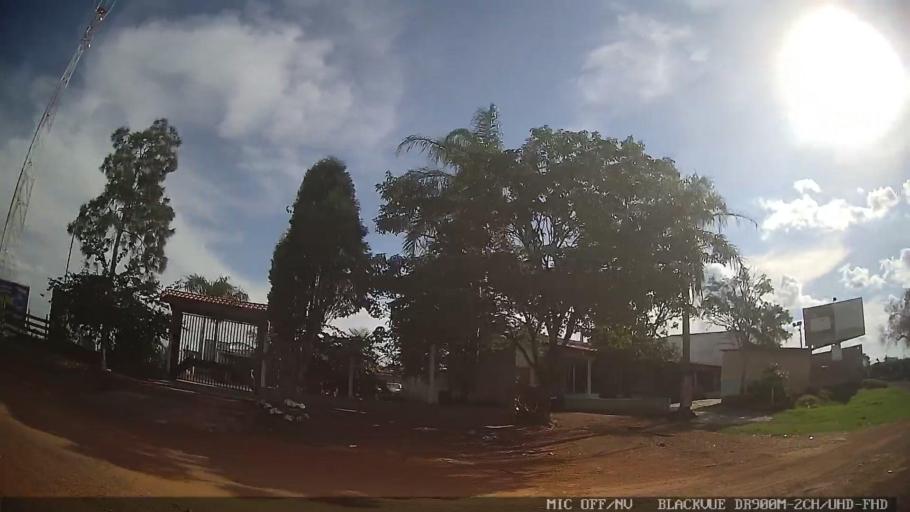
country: BR
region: Sao Paulo
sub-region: Laranjal Paulista
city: Laranjal Paulista
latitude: -23.0794
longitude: -47.7926
